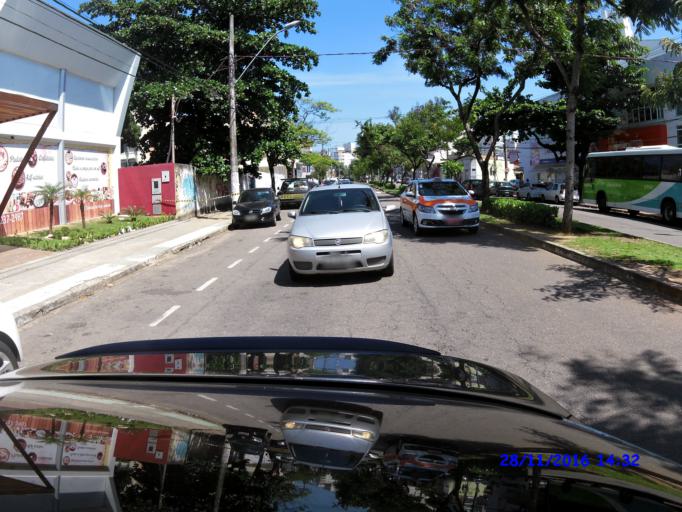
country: BR
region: Espirito Santo
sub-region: Vila Velha
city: Vila Velha
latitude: -20.2576
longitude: -40.2665
